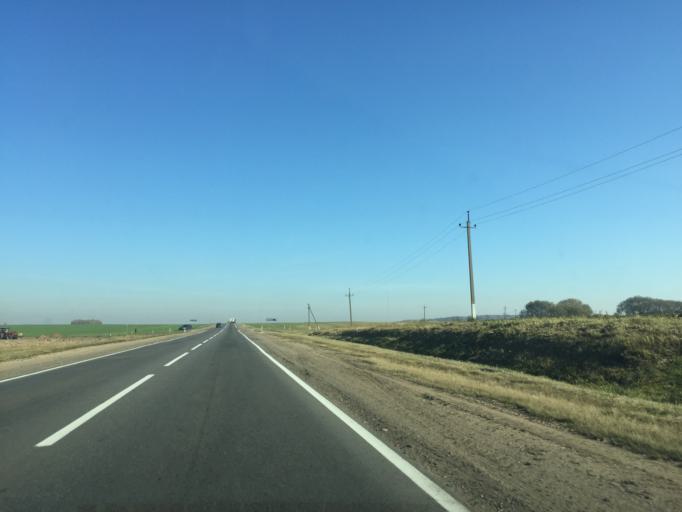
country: BY
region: Mogilev
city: Buynichy
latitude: 53.9587
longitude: 30.2390
